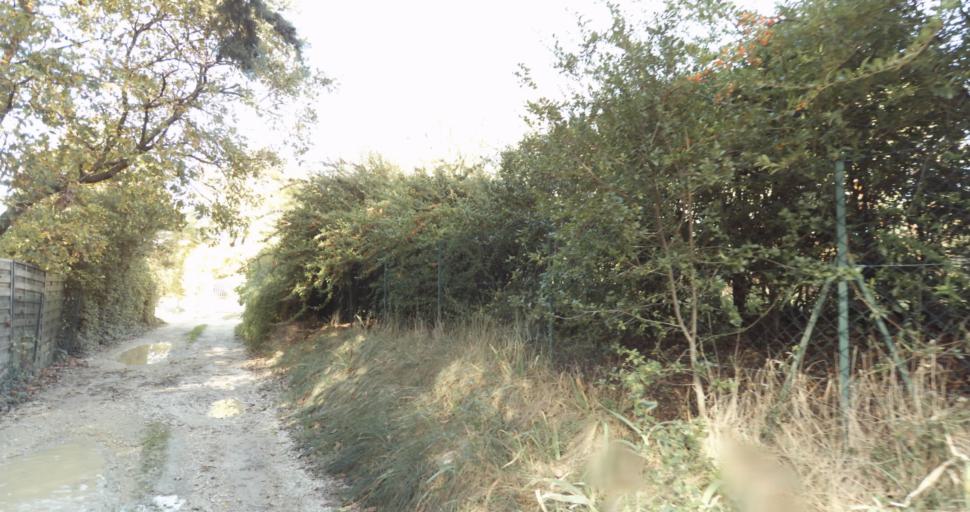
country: FR
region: Provence-Alpes-Cote d'Azur
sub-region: Departement des Bouches-du-Rhone
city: Venelles
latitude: 43.6076
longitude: 5.4906
